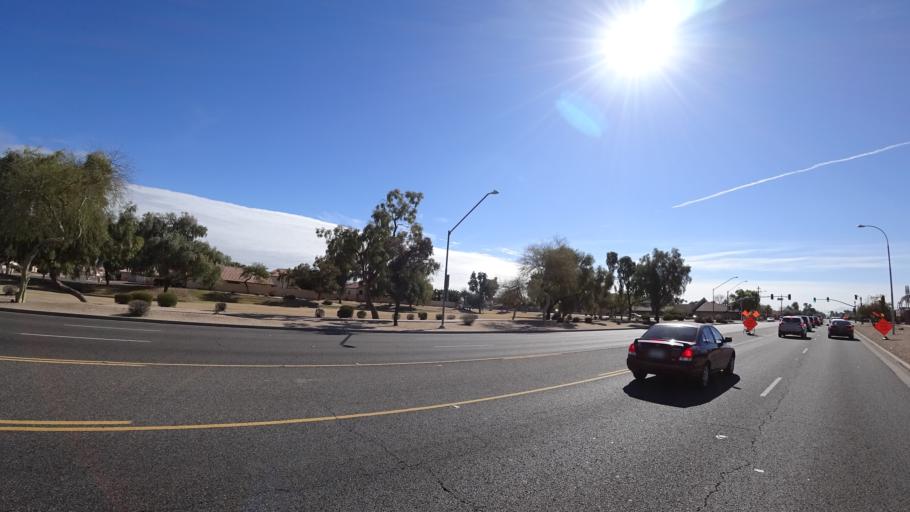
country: US
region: Arizona
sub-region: Maricopa County
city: Glendale
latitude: 33.5758
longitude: -112.1863
